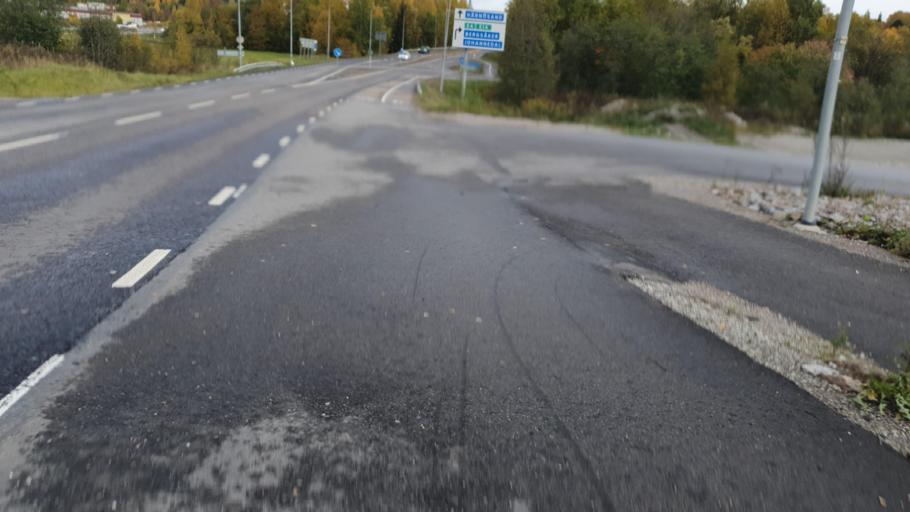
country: SE
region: Vaesternorrland
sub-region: Sundsvalls Kommun
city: Sundsbruk
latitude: 62.4448
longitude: 17.3416
